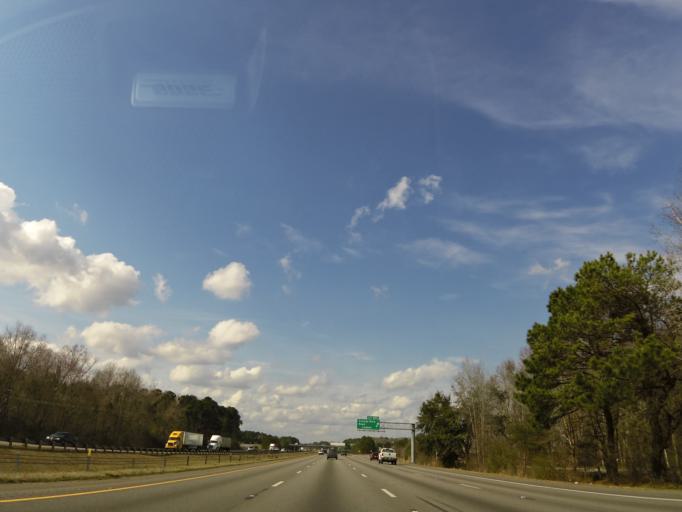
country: US
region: South Carolina
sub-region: Berkeley County
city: Ladson
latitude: 32.9947
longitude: -80.0897
